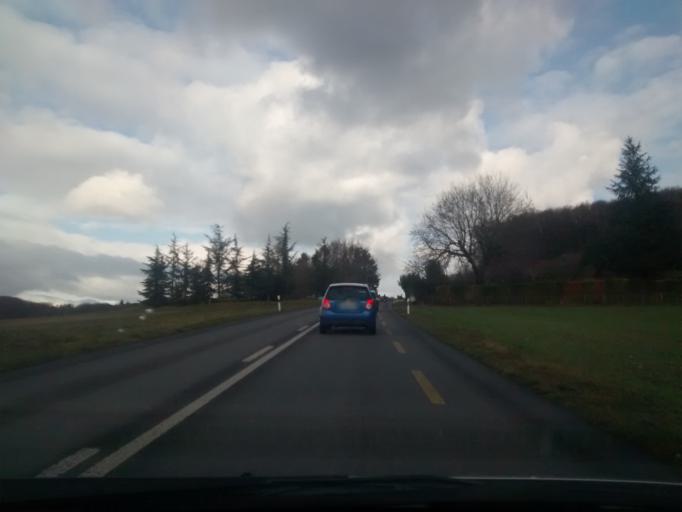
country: CH
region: Vaud
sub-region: Ouest Lausannois District
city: Crissier
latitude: 46.5645
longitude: 6.5781
